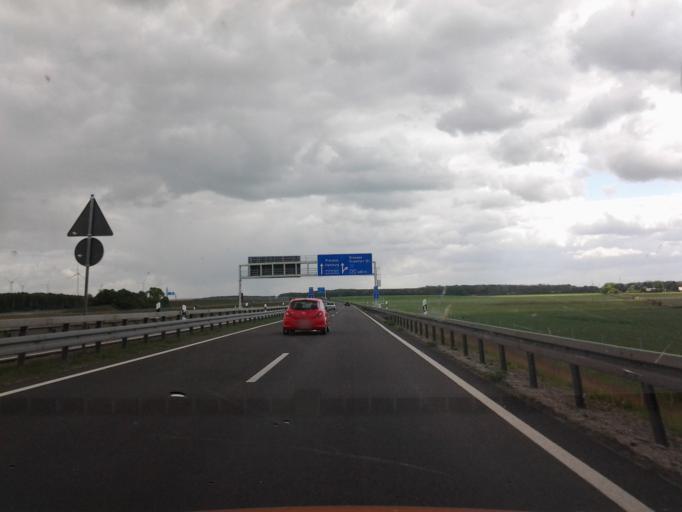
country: DE
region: Berlin
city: Falkenberg
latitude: 52.6130
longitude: 13.5453
